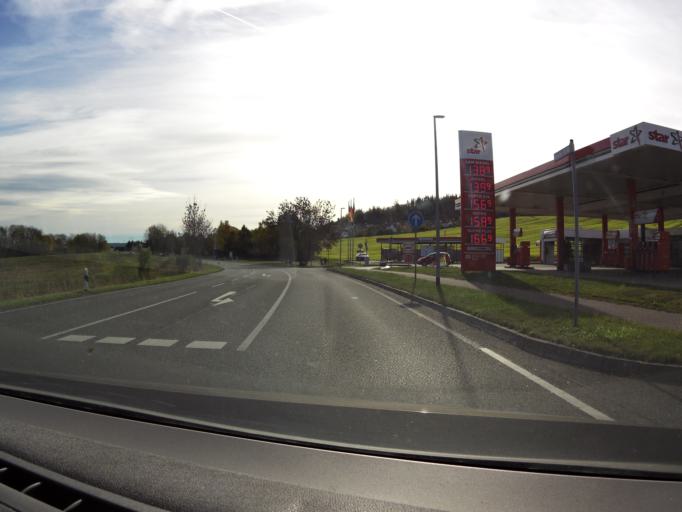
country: DE
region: Thuringia
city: Ilmenau
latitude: 50.6935
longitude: 10.9009
